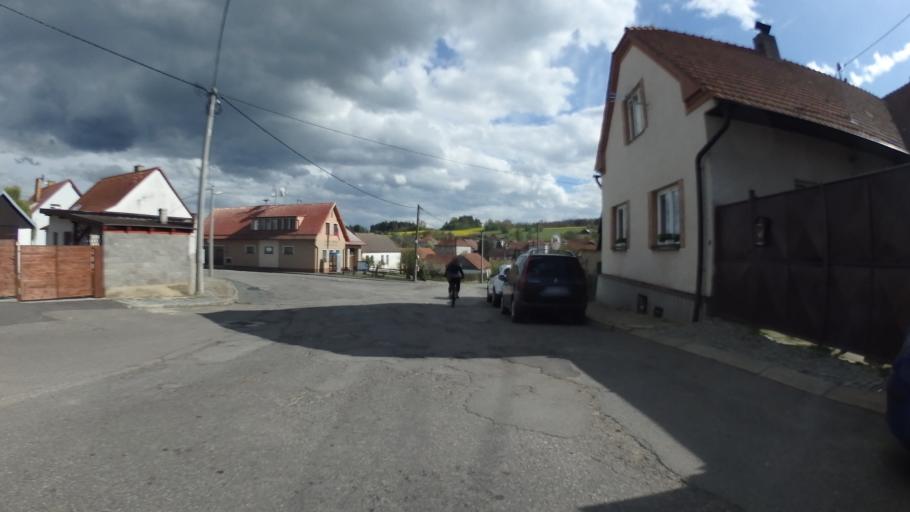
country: CZ
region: Vysocina
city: Merin
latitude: 49.3486
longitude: 15.8781
